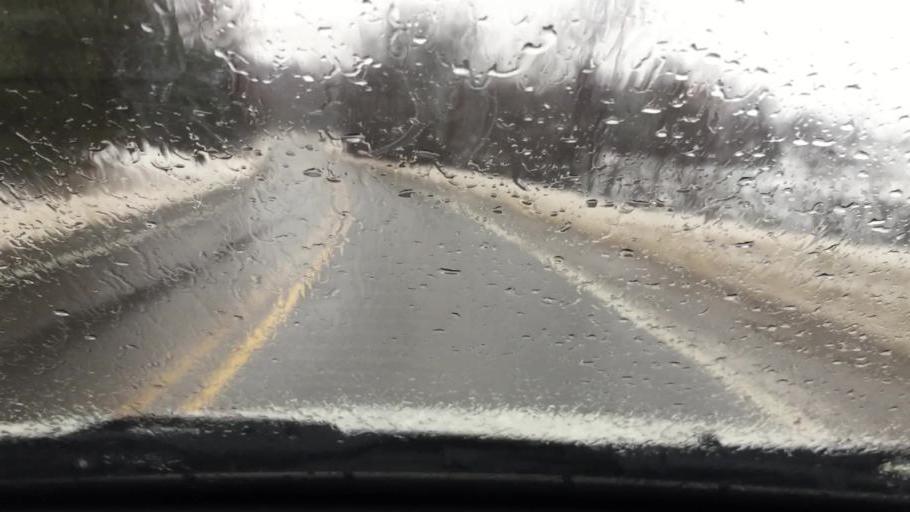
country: US
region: Michigan
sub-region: Charlevoix County
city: Charlevoix
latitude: 45.2487
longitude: -85.1813
